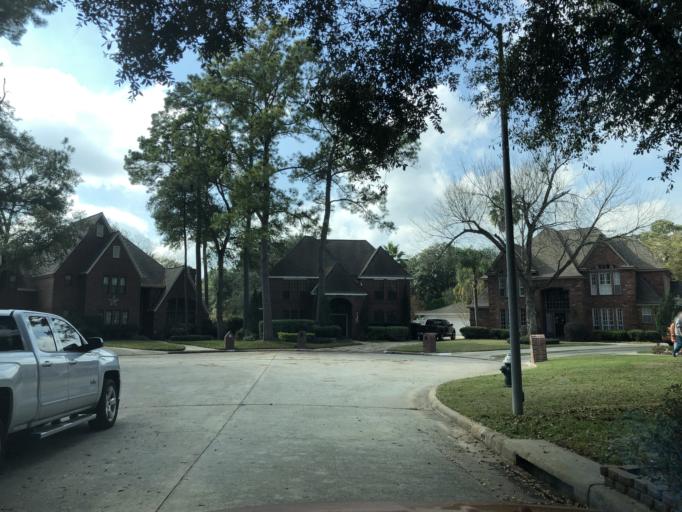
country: US
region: Texas
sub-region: Harris County
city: Tomball
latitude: 30.0292
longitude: -95.5460
